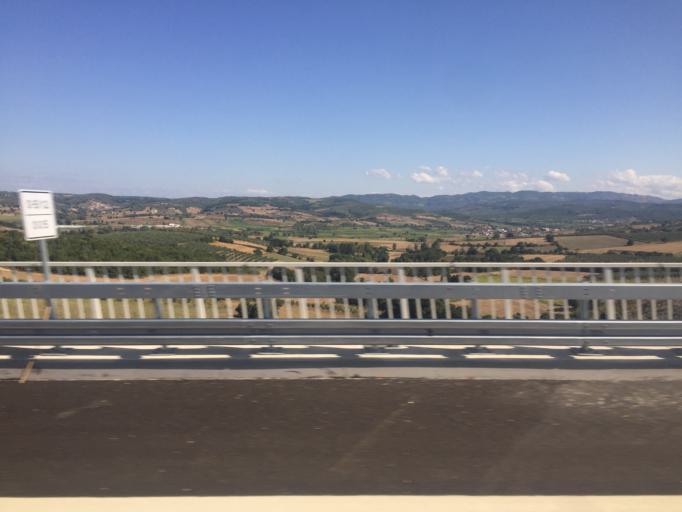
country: TR
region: Bursa
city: Gorukle
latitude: 40.2563
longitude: 28.7324
